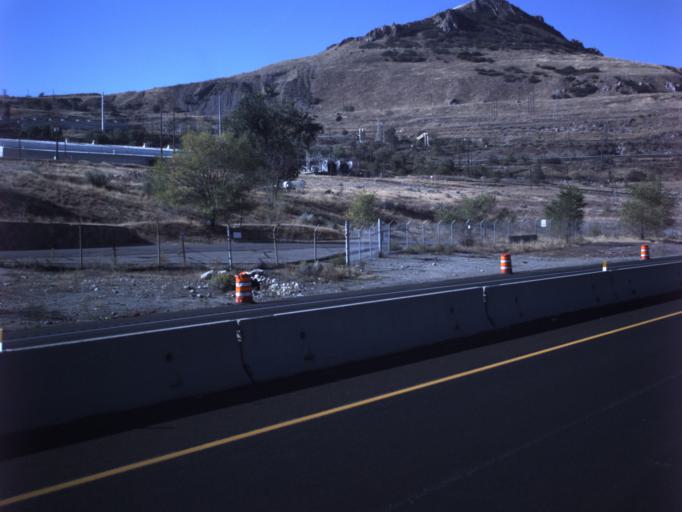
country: US
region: Utah
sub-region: Salt Lake County
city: Magna
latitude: 40.7168
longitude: -112.1219
